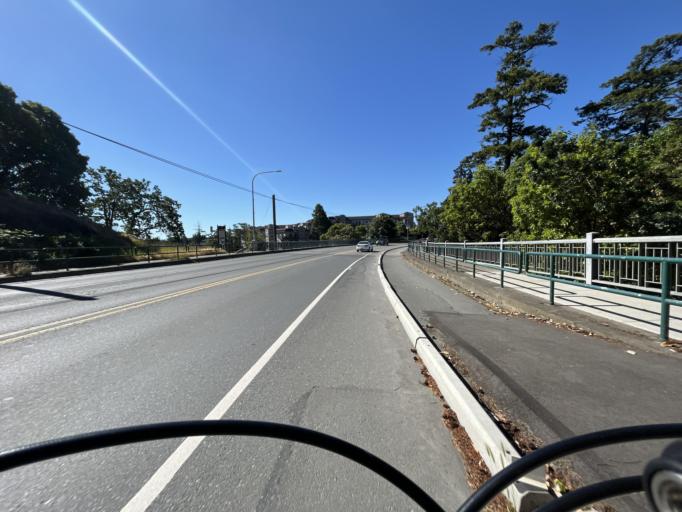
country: CA
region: British Columbia
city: Victoria
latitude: 48.4469
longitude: -123.4004
